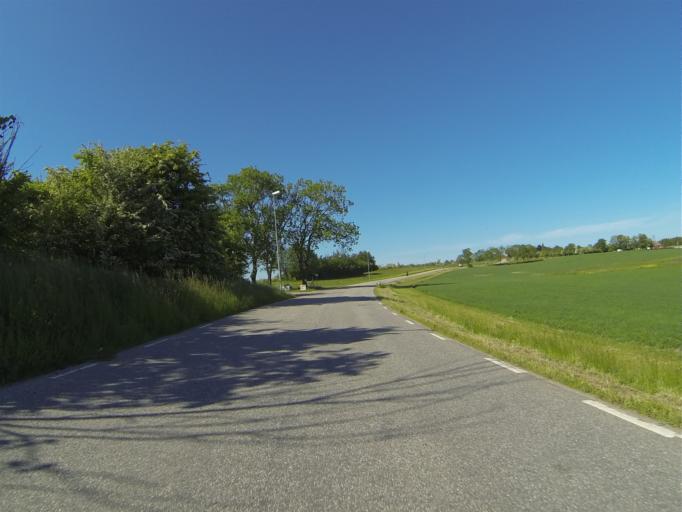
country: SE
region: Skane
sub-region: Malmo
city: Oxie
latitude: 55.5892
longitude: 13.1228
